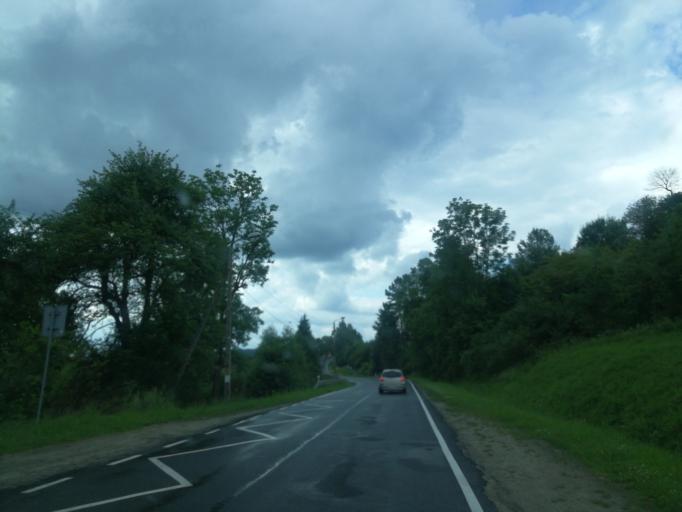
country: PL
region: Subcarpathian Voivodeship
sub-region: Powiat leski
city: Olszanica
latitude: 49.4362
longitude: 22.4557
